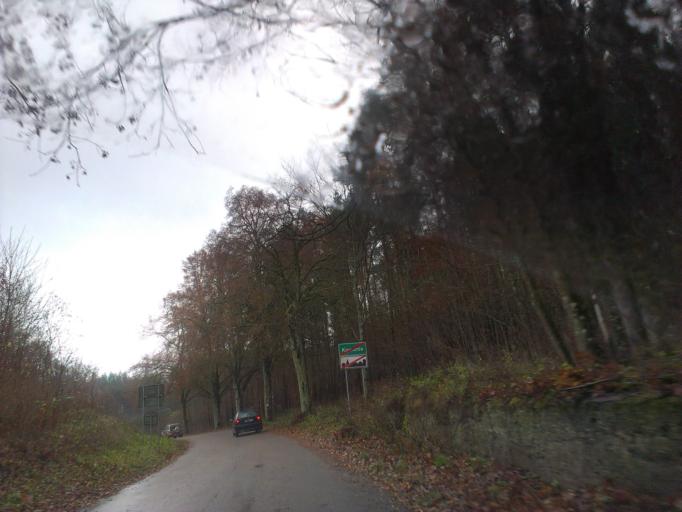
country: PL
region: West Pomeranian Voivodeship
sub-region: Powiat szczecinecki
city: Lubowo
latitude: 53.6283
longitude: 16.3449
